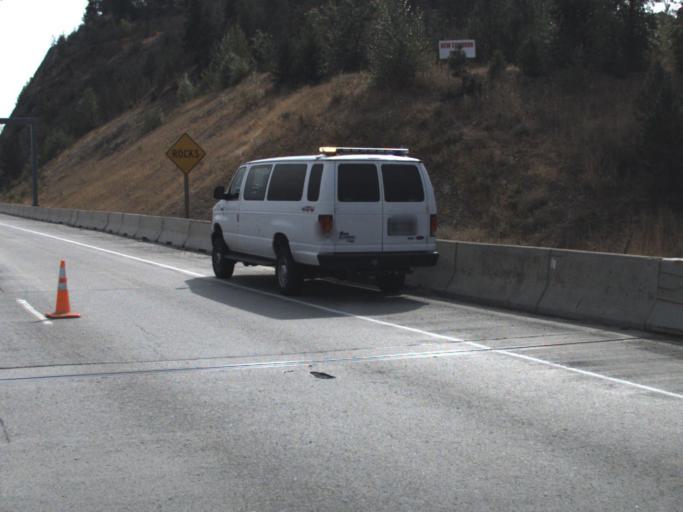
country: US
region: Washington
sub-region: Spokane County
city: Fairwood
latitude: 47.7835
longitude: -117.4048
